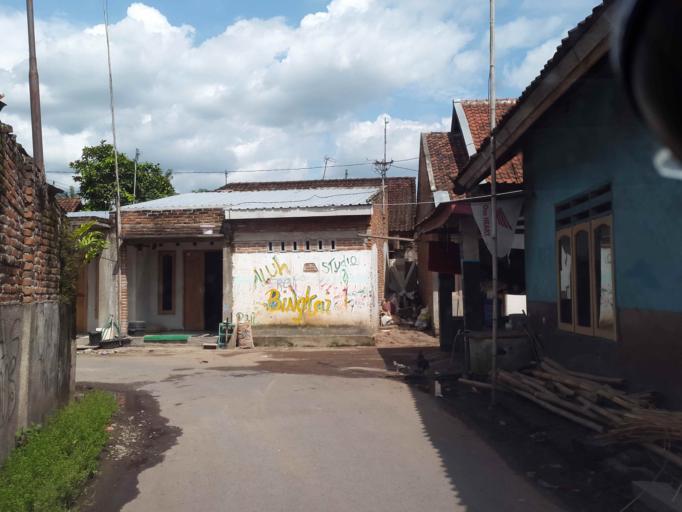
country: ID
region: West Nusa Tenggara
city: Mambalan
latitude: -8.5426
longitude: 116.1035
